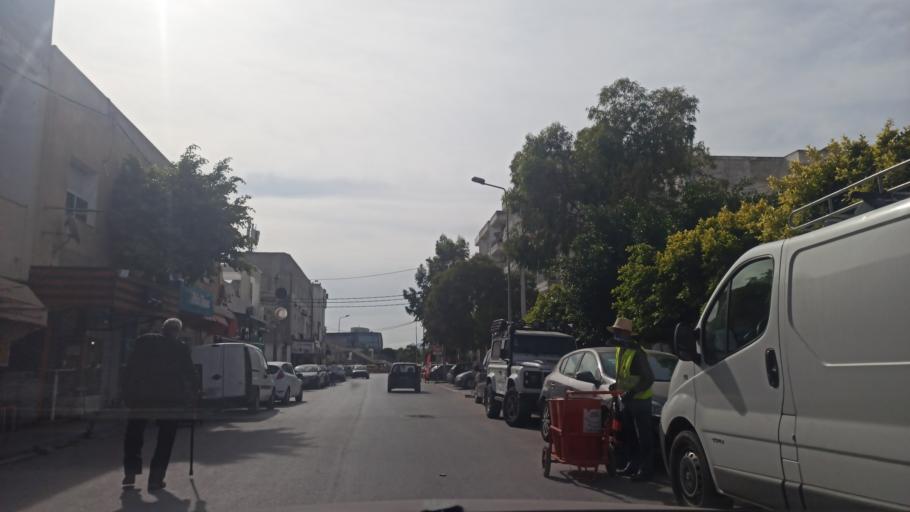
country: TN
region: Tunis
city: La Goulette
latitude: 36.8502
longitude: 10.2631
